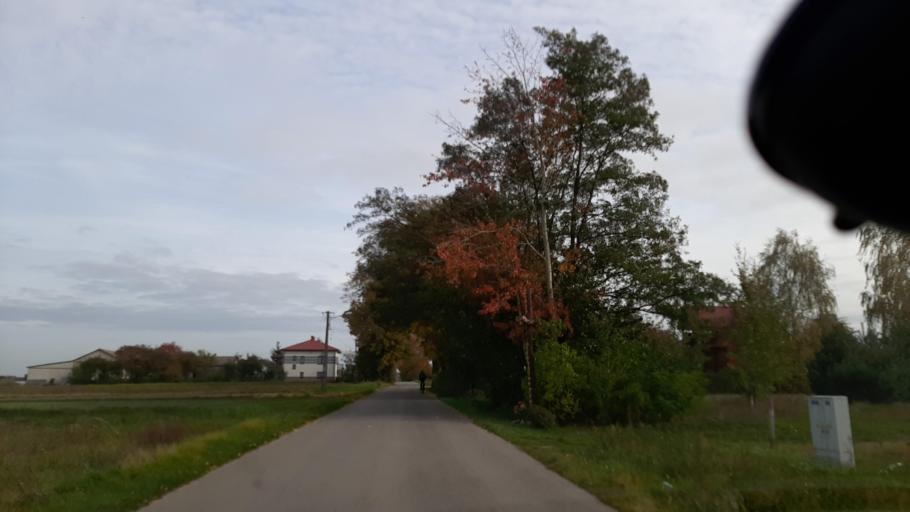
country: PL
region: Lublin Voivodeship
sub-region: Powiat lubelski
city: Garbow
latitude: 51.3971
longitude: 22.3399
